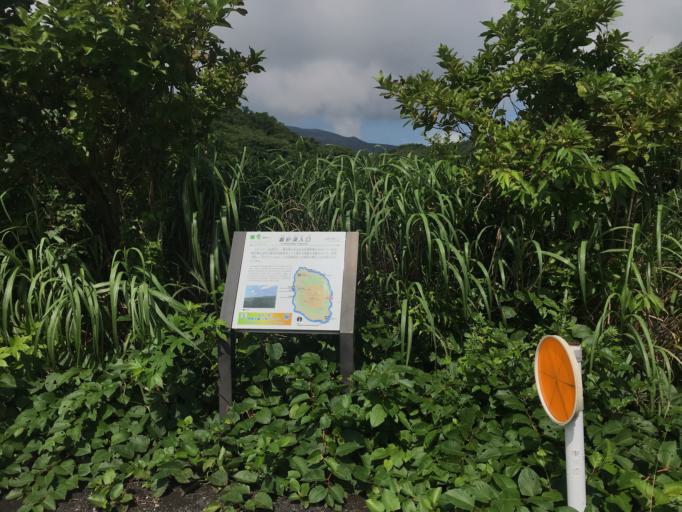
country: JP
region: Shizuoka
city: Ito
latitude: 34.7298
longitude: 139.4344
